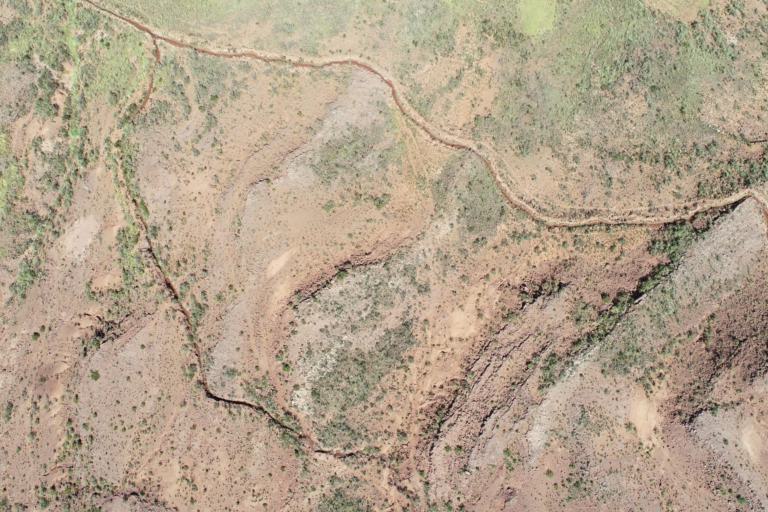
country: BO
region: La Paz
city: Tiahuanaco
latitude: -16.5992
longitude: -68.7569
